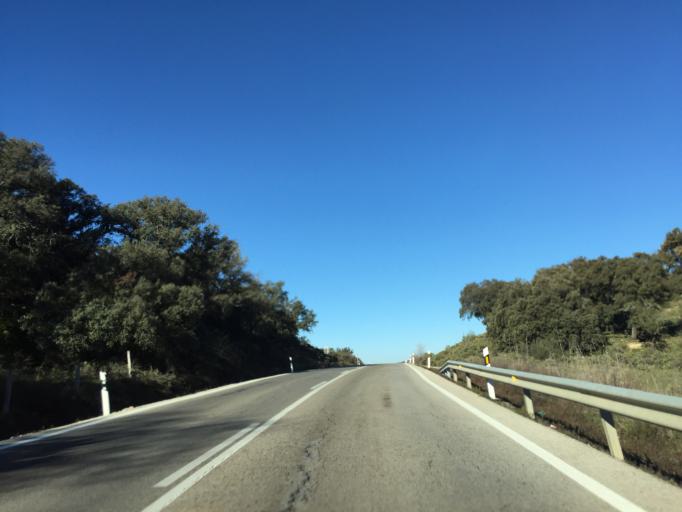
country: ES
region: Andalusia
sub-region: Provincia de Malaga
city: Cuevas del Becerro
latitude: 36.8321
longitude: -5.0702
